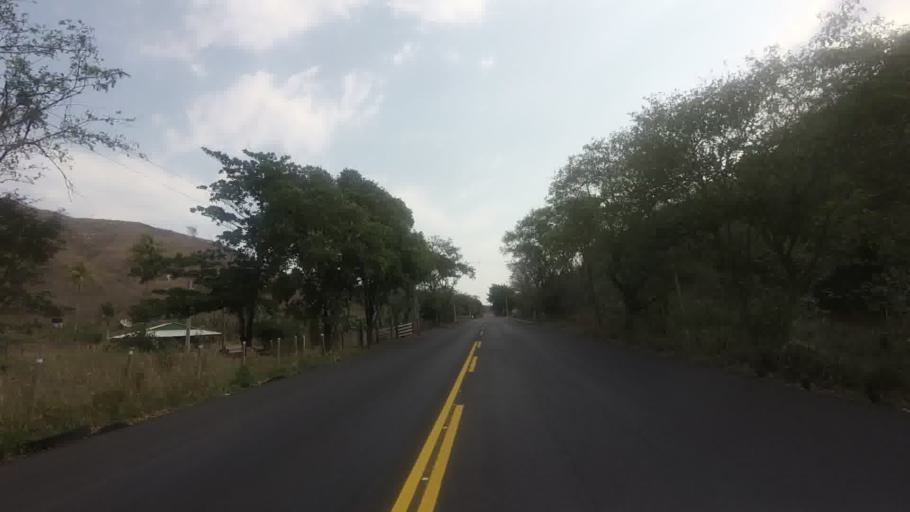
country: BR
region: Rio de Janeiro
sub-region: Bom Jesus Do Itabapoana
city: Bom Jesus do Itabapoana
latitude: -21.2345
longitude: -41.7493
